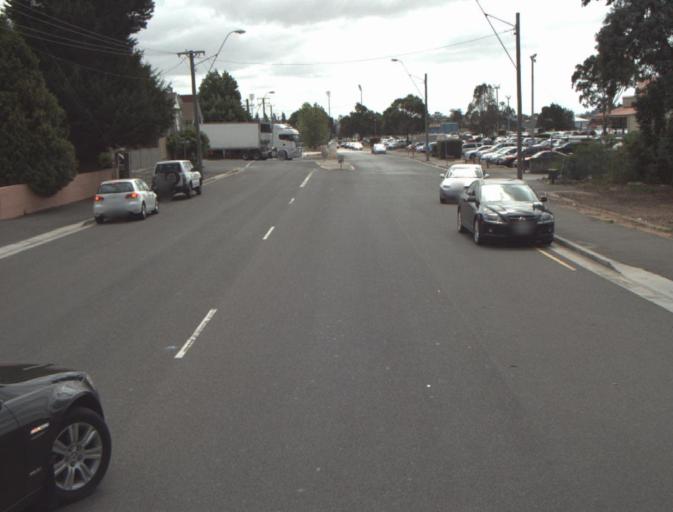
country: AU
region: Tasmania
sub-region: Launceston
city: East Launceston
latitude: -41.4307
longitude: 147.1490
